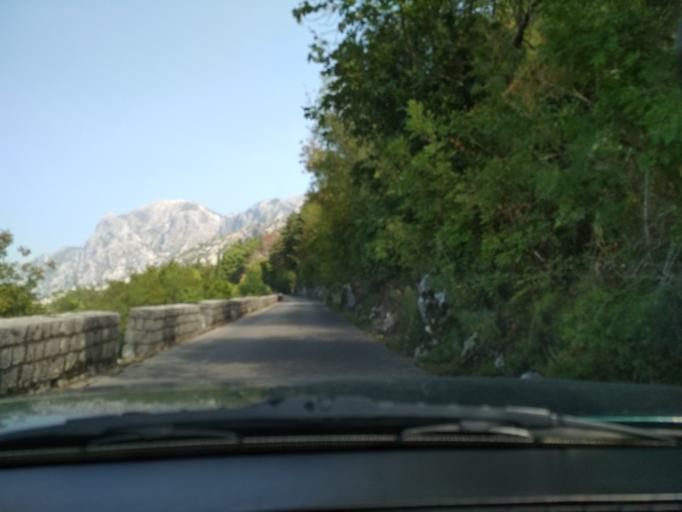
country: ME
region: Kotor
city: Kotor
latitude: 42.4040
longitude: 18.7757
